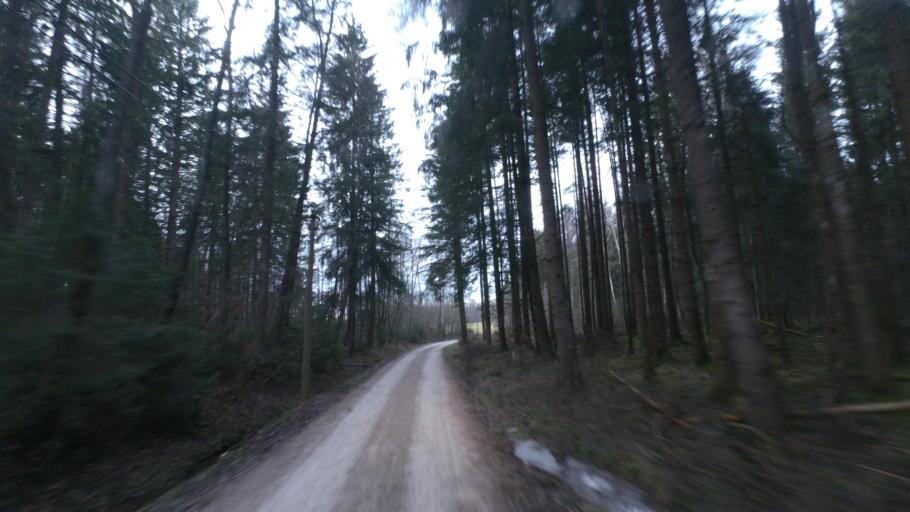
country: DE
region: Bavaria
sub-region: Upper Bavaria
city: Ubersee
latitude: 47.8114
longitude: 12.5128
